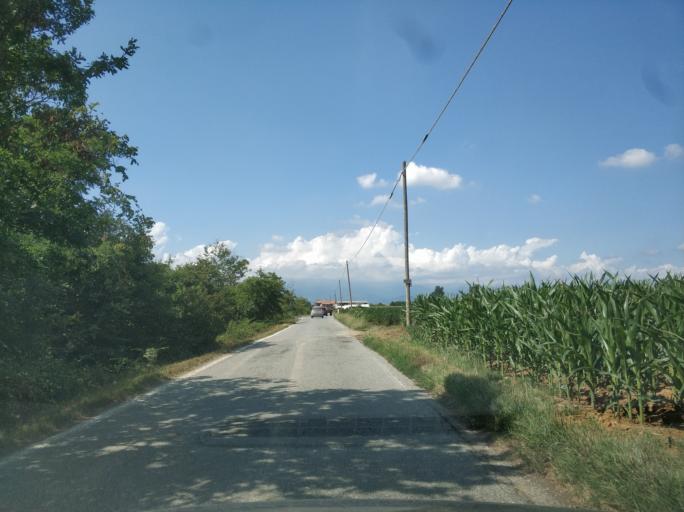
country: IT
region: Piedmont
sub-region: Provincia di Torino
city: Rivarossa
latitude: 45.2763
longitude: 7.7295
